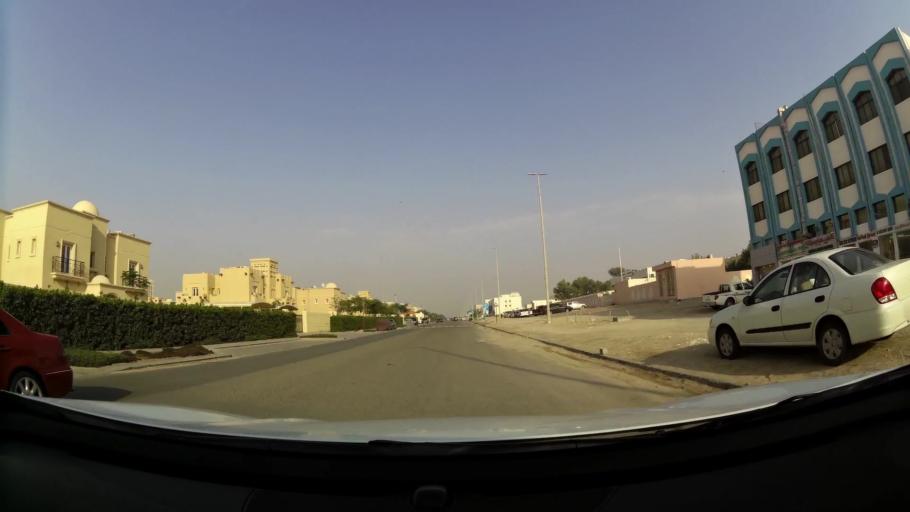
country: AE
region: Abu Dhabi
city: Abu Dhabi
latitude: 24.2984
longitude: 54.6213
